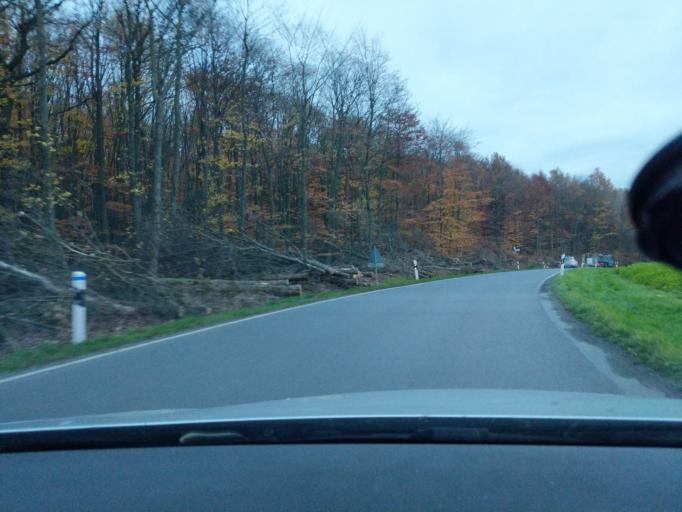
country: DE
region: North Rhine-Westphalia
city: Datteln
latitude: 51.6686
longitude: 7.4089
